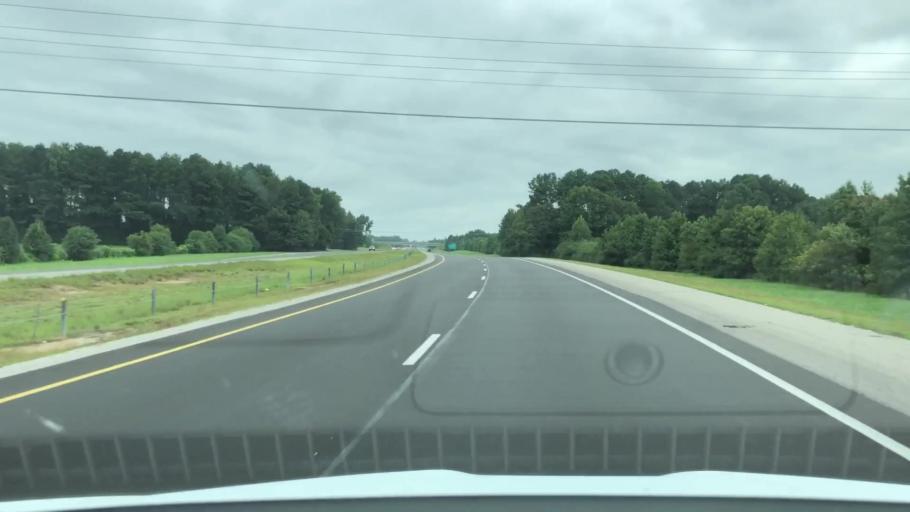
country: US
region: North Carolina
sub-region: Wayne County
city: Fremont
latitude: 35.5969
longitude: -77.9811
